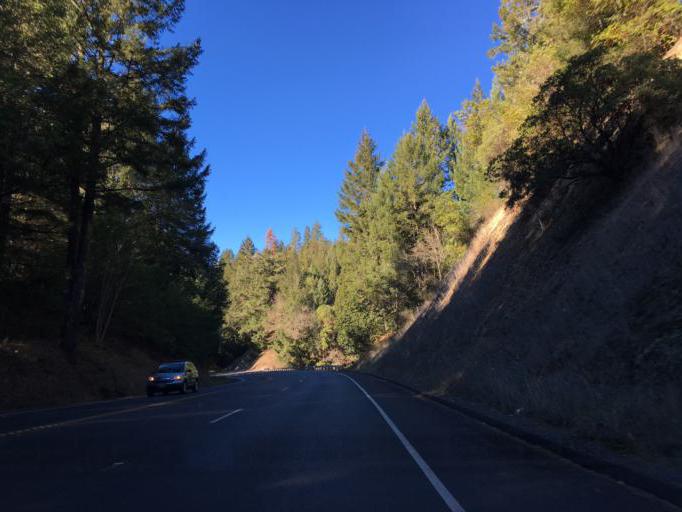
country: US
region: California
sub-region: Mendocino County
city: Brooktrails
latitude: 39.4674
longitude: -123.3543
